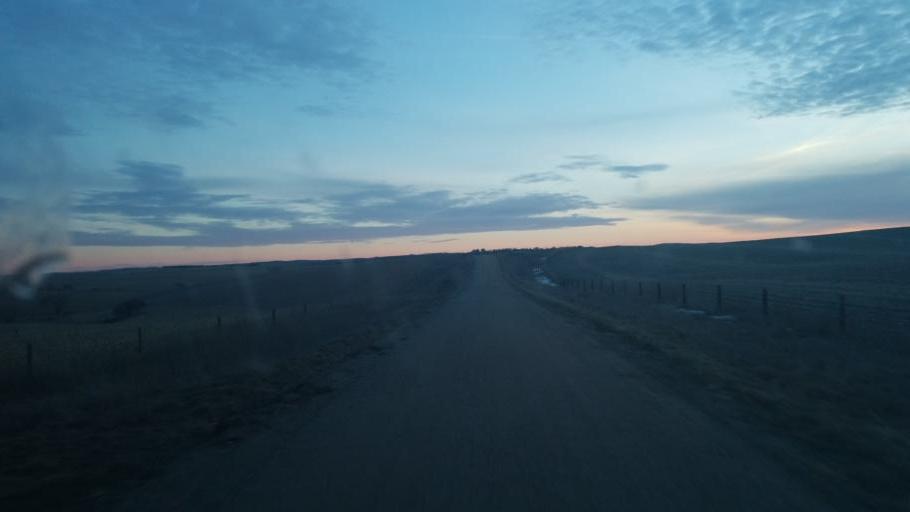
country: US
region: Nebraska
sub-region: Knox County
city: Center
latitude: 42.6443
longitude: -97.7992
